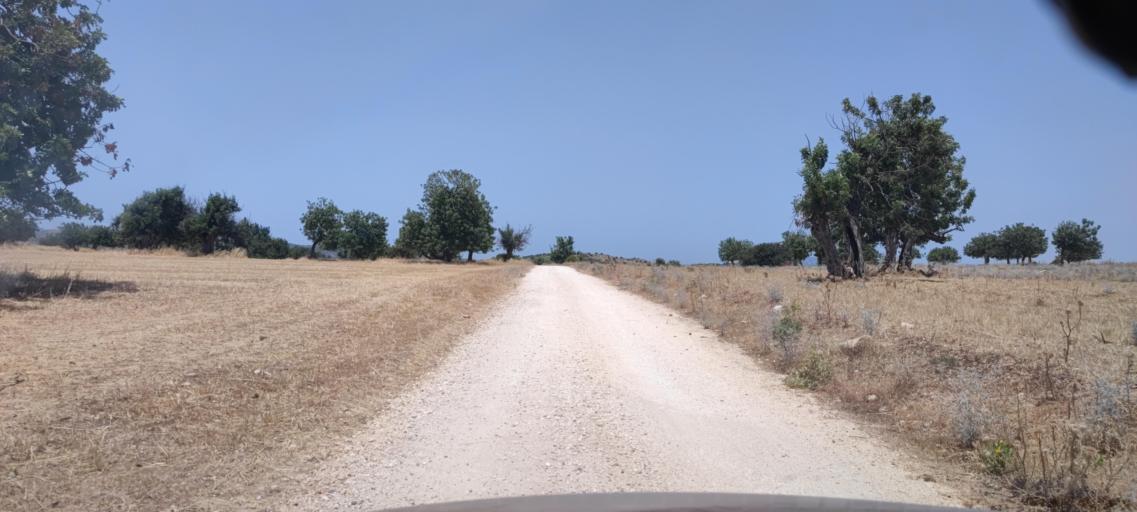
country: CY
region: Limassol
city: Pissouri
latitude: 34.7243
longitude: 32.5929
